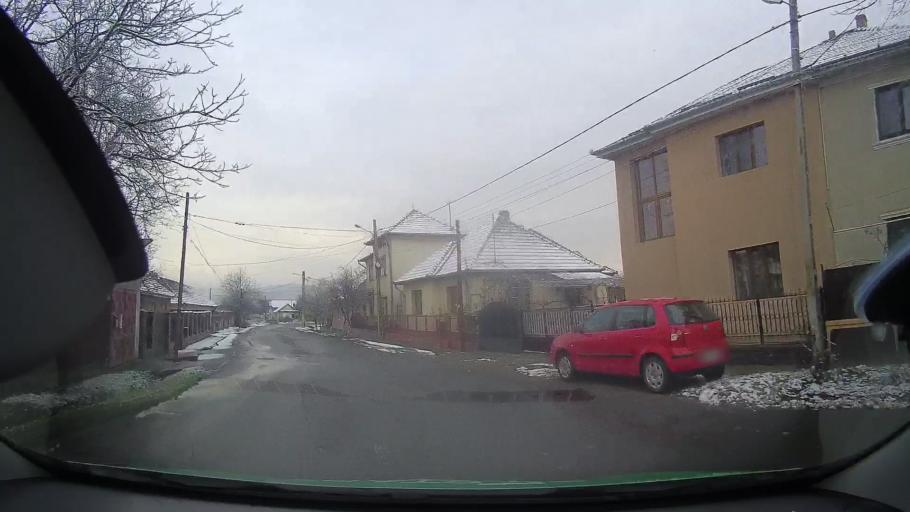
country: RO
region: Mures
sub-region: Comuna Ludus
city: Ludus
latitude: 46.4650
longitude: 24.0864
